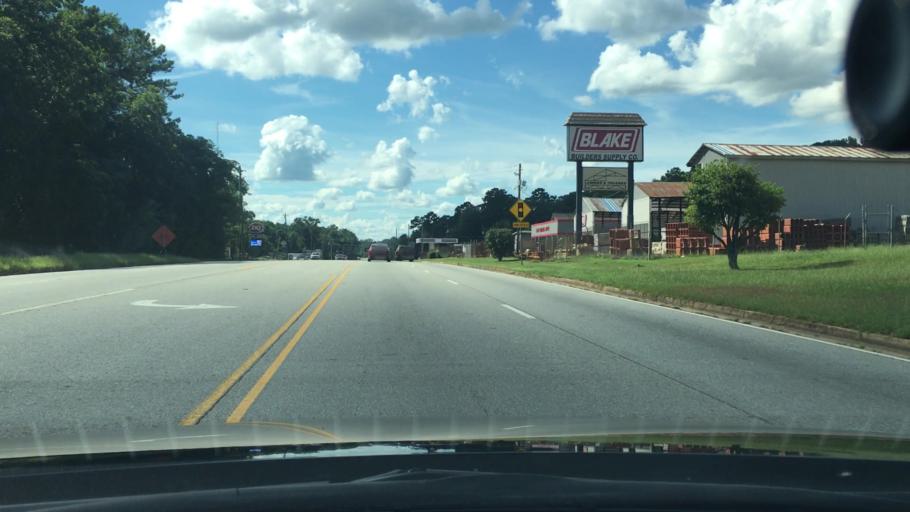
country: US
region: Georgia
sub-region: Spalding County
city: East Griffin
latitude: 33.2369
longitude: -84.2435
